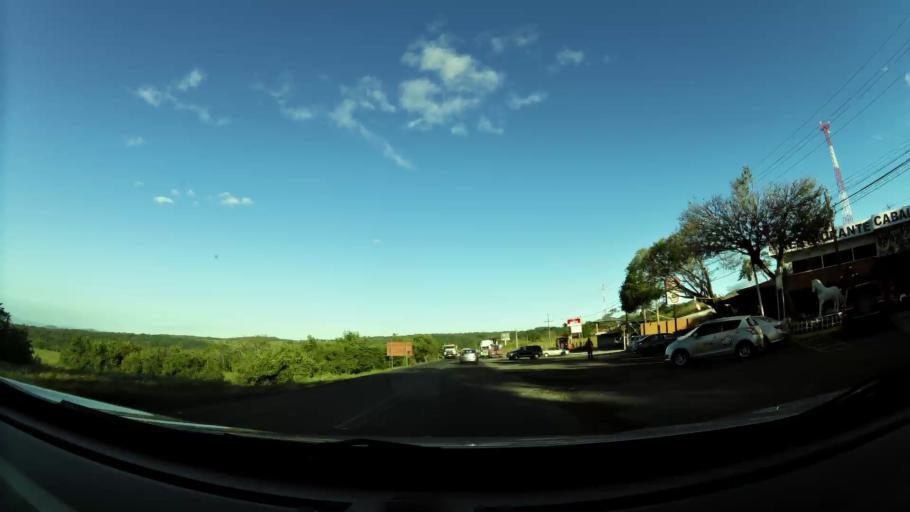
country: CR
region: Puntarenas
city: Miramar
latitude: 10.0947
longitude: -84.7995
